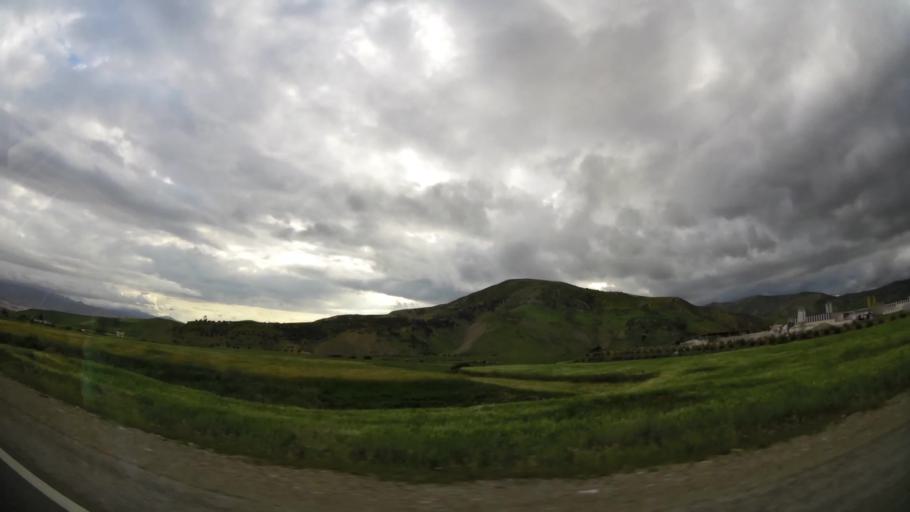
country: MA
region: Taza-Al Hoceima-Taounate
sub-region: Taza
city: Taza
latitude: 34.2775
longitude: -3.9562
